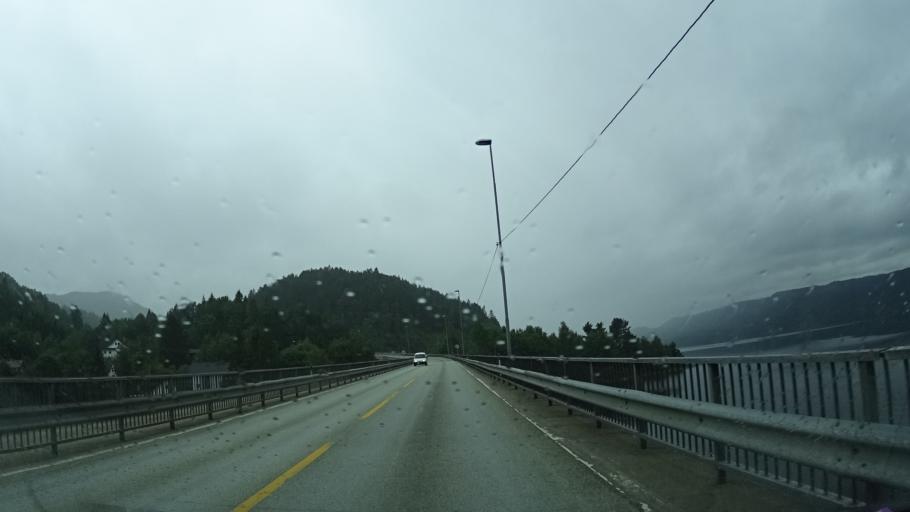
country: NO
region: Rogaland
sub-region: Lund
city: Moi
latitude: 58.4053
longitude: 6.6227
